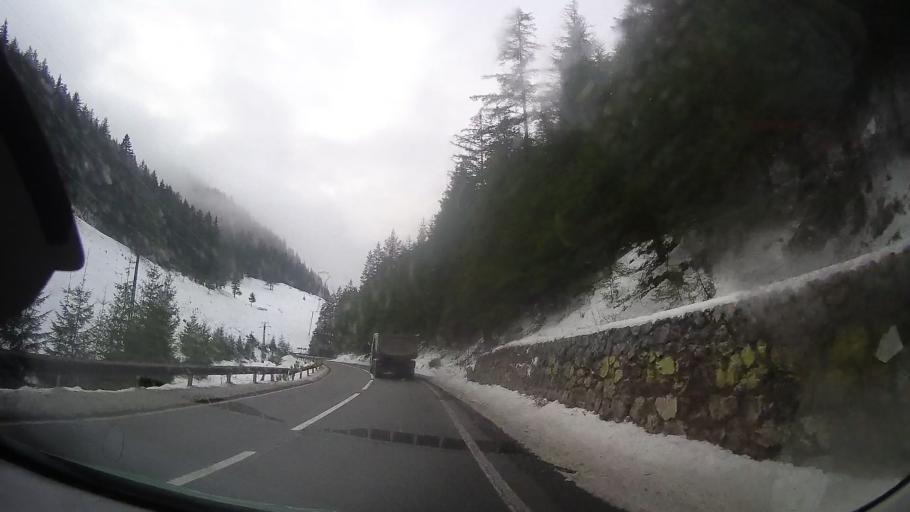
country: RO
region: Neamt
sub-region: Comuna Bicaz Chei
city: Bicaz Chei
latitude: 46.7782
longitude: 25.7629
